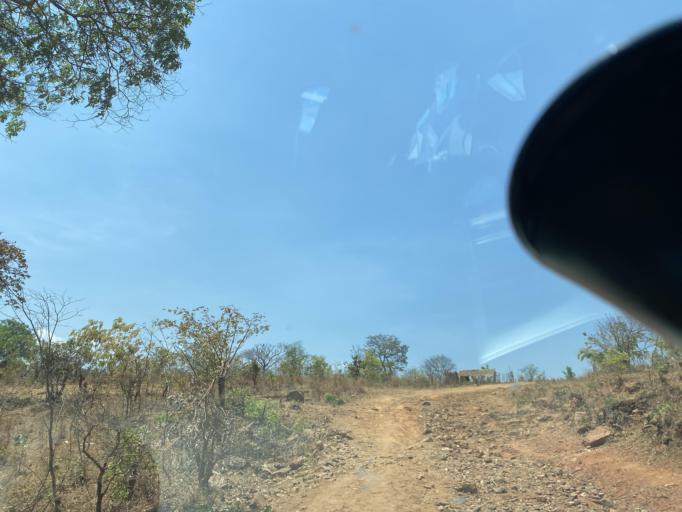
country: ZM
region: Lusaka
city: Kafue
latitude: -15.8052
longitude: 28.4412
